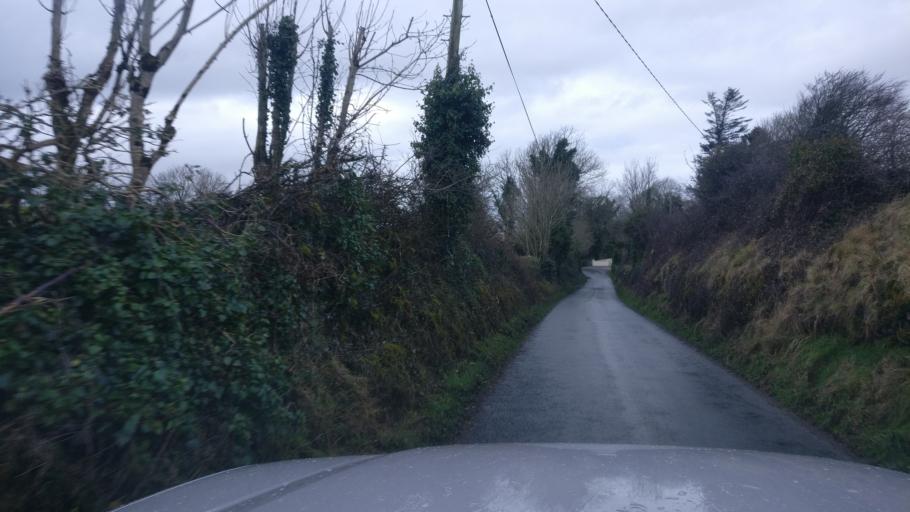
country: IE
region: Connaught
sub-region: County Galway
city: Athenry
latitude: 53.1851
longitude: -8.7060
